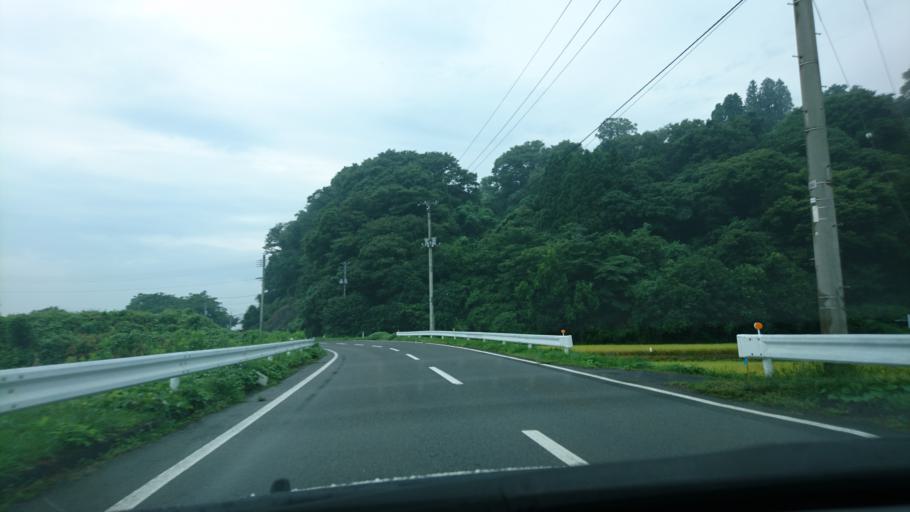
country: JP
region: Iwate
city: Ichinoseki
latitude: 38.8893
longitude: 141.2664
